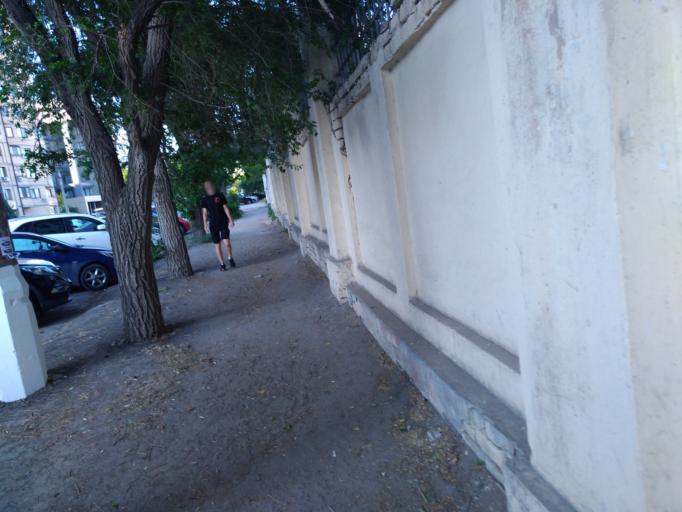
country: RU
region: Volgograd
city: Volgograd
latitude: 48.7115
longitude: 44.5038
